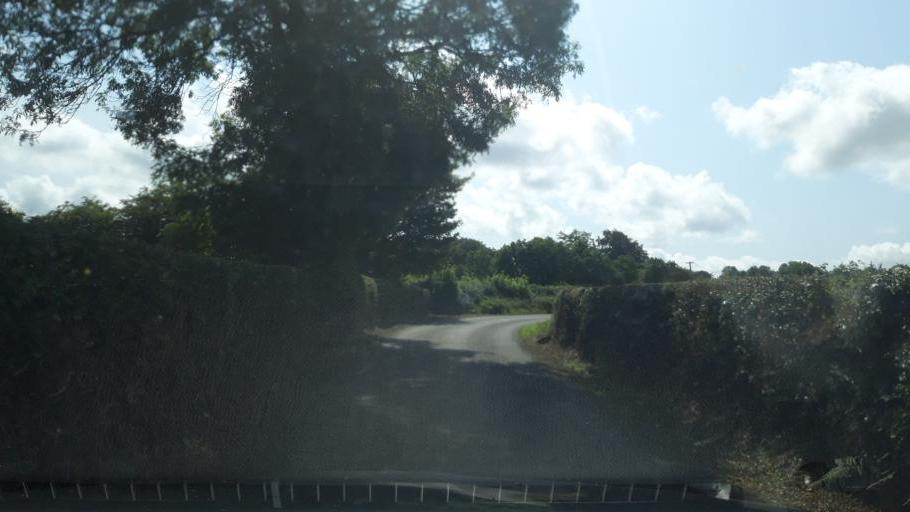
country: IE
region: Leinster
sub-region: Kilkenny
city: Graiguenamanagh
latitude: 52.5753
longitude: -6.9848
